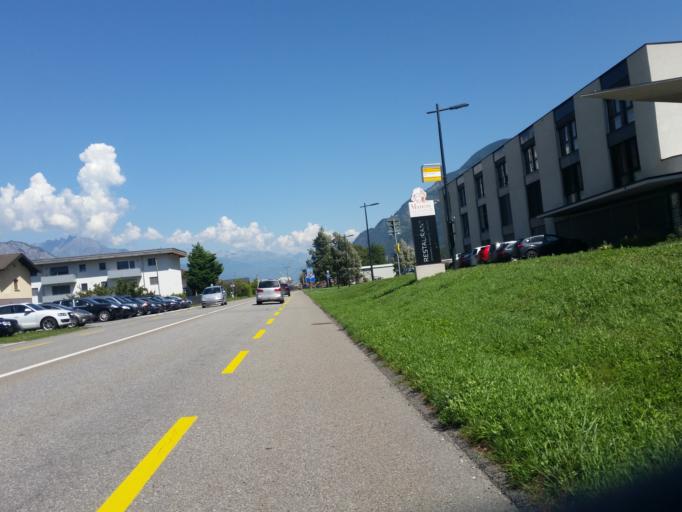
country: CH
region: Valais
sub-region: Martigny District
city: Saxon
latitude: 46.1442
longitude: 7.1641
